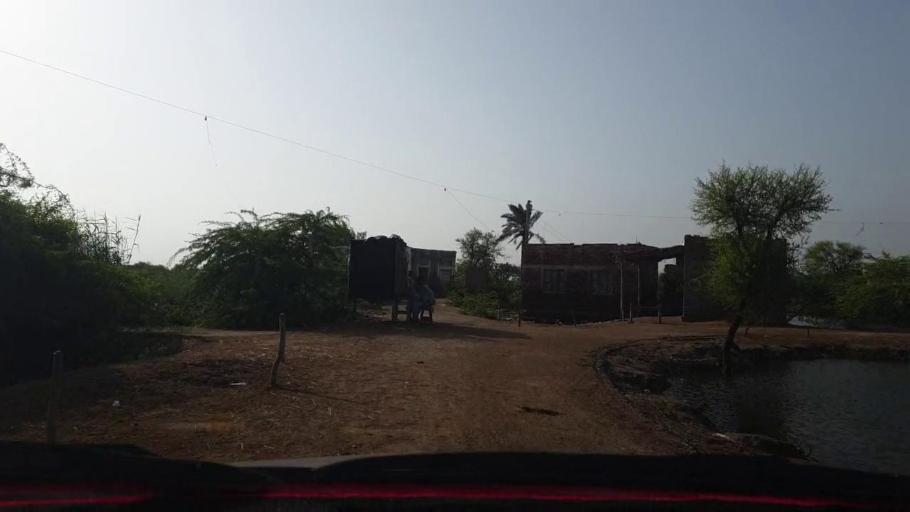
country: PK
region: Sindh
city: Talhar
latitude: 24.9247
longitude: 68.7514
